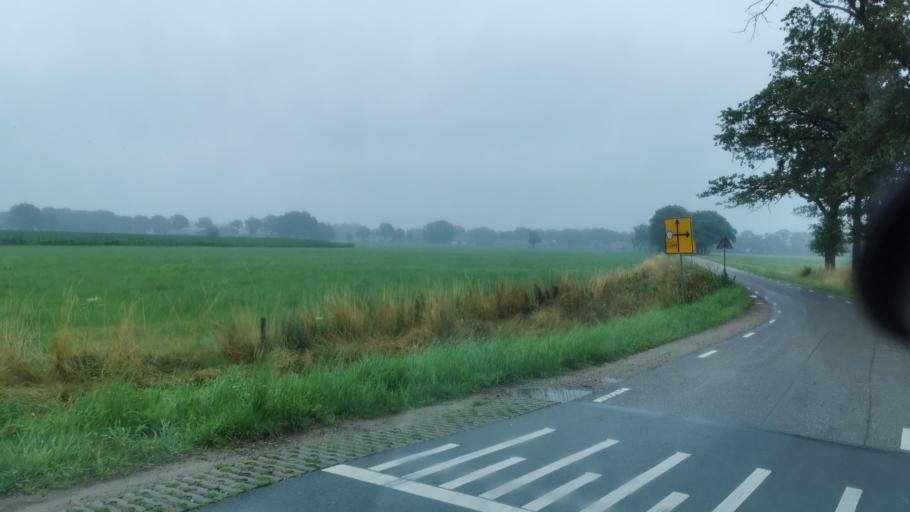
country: NL
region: Overijssel
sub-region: Gemeente Losser
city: Losser
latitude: 52.2503
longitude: 6.9819
